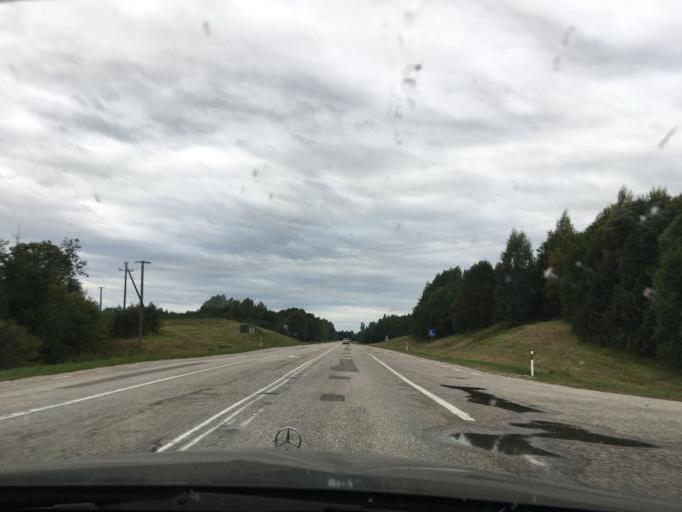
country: LV
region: Aluksnes Rajons
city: Aluksne
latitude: 57.5926
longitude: 27.0869
